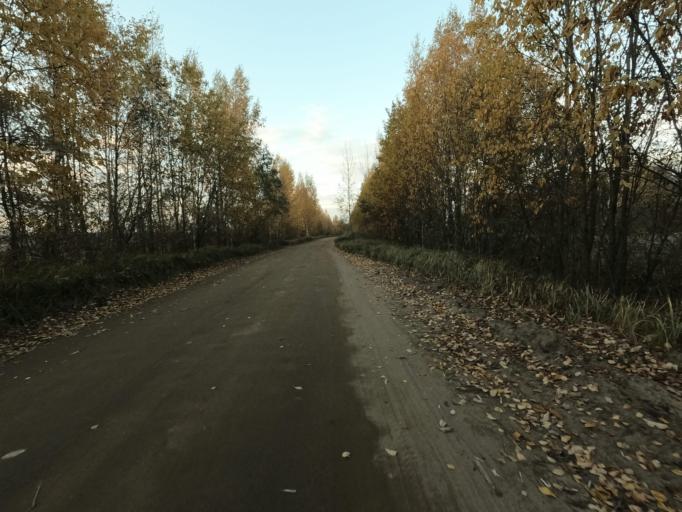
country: RU
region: Leningrad
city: Mga
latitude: 59.7960
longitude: 31.2003
